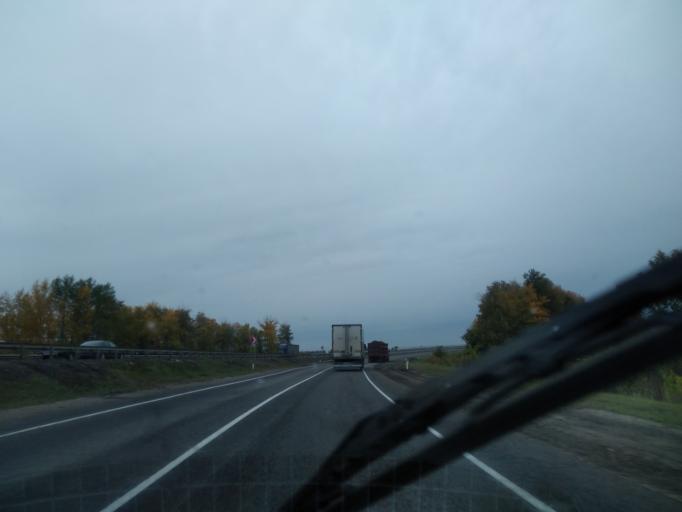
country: RU
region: Lipetsk
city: Zadonsk
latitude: 52.4450
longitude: 38.7861
